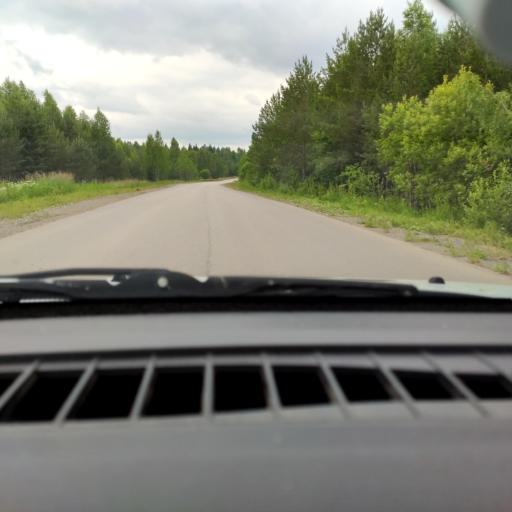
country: RU
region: Perm
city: Orda
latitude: 57.1260
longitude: 56.6853
